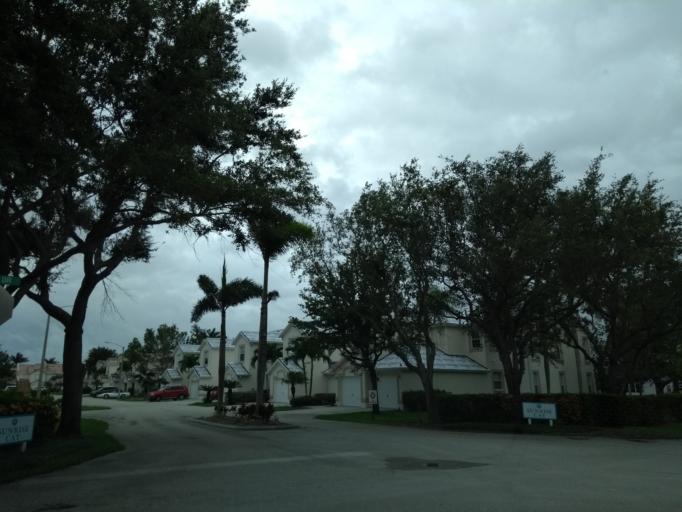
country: US
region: Florida
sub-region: Collier County
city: Marco
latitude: 25.9548
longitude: -81.5124
